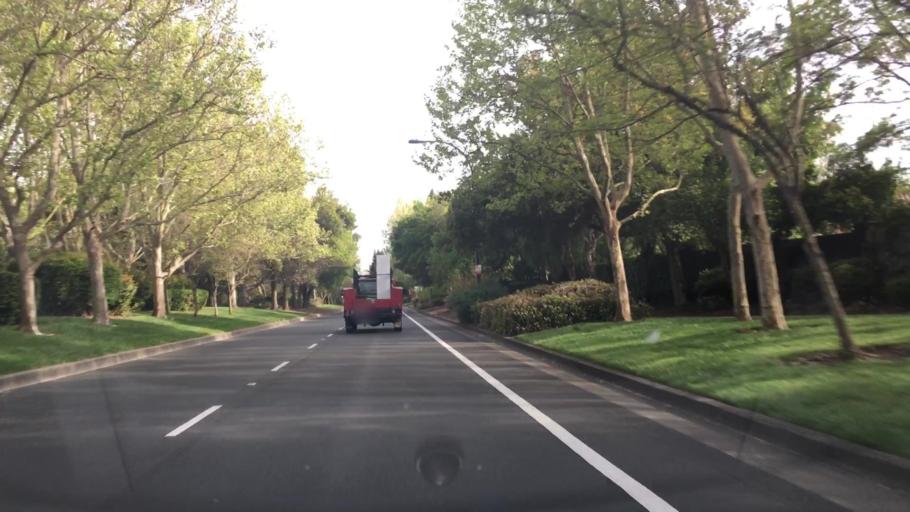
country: US
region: California
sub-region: Solano County
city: Green Valley
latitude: 38.2250
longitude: -122.1464
